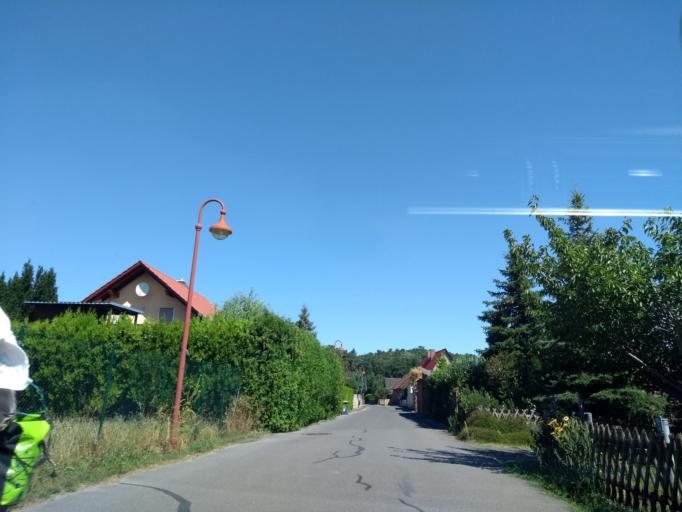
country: DE
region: Brandenburg
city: Lubbenau
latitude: 51.8352
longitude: 13.9502
